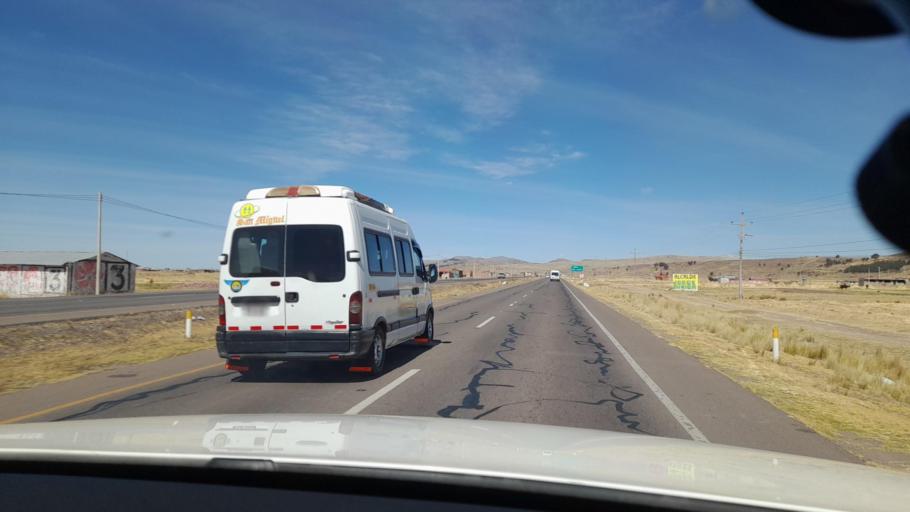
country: PE
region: Puno
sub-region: Provincia de Puno
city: Paucarcolla
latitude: -15.7094
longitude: -70.0644
